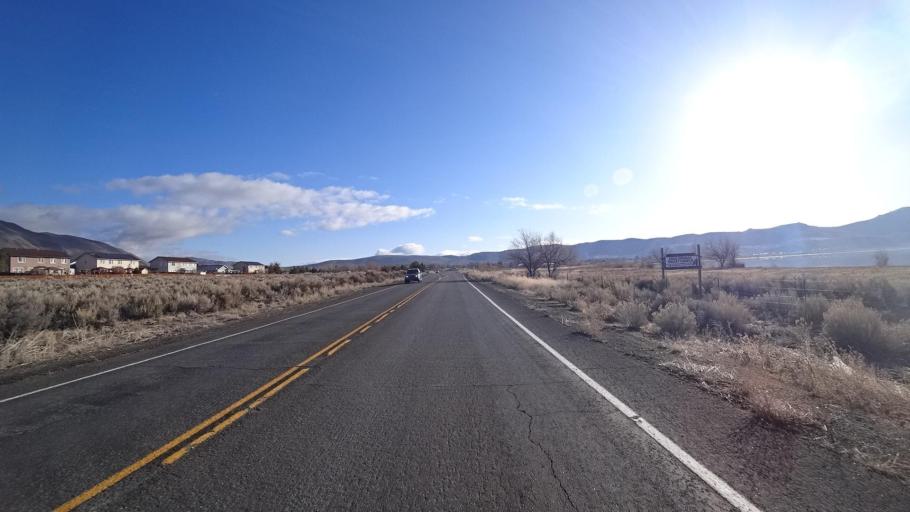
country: US
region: Nevada
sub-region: Washoe County
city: Cold Springs
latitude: 39.6738
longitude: -119.9835
